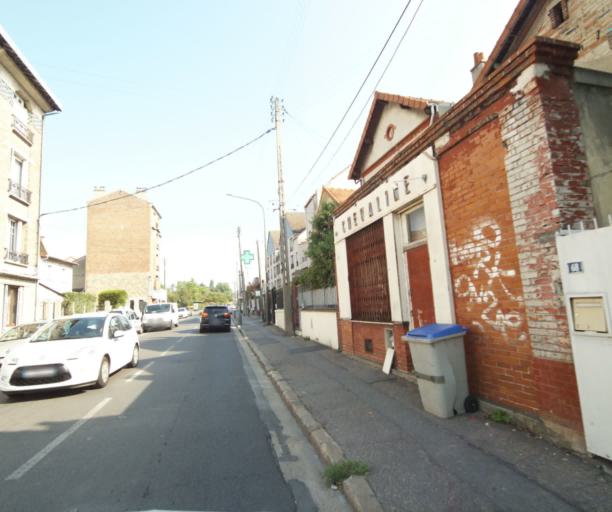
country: FR
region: Ile-de-France
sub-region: Departement du Val-d'Oise
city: Argenteuil
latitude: 48.9510
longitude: 2.2441
